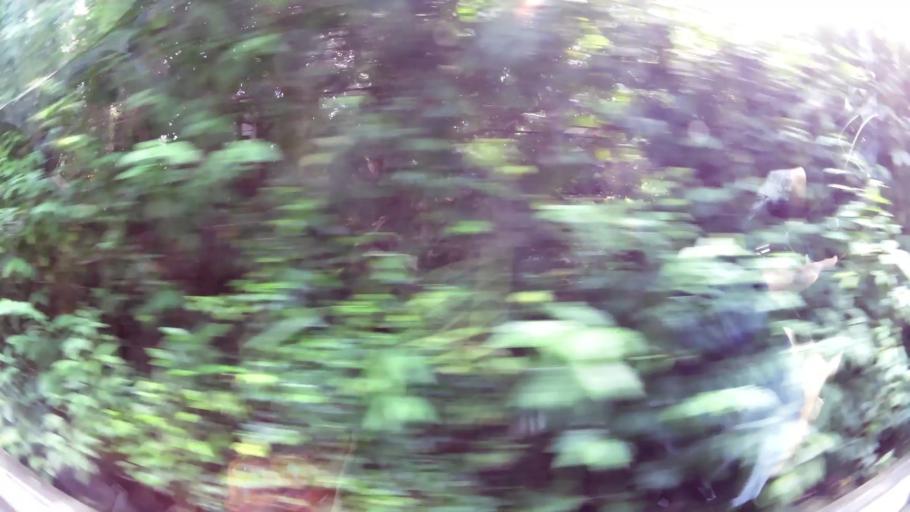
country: SG
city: Singapore
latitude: 1.2720
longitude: 103.8124
